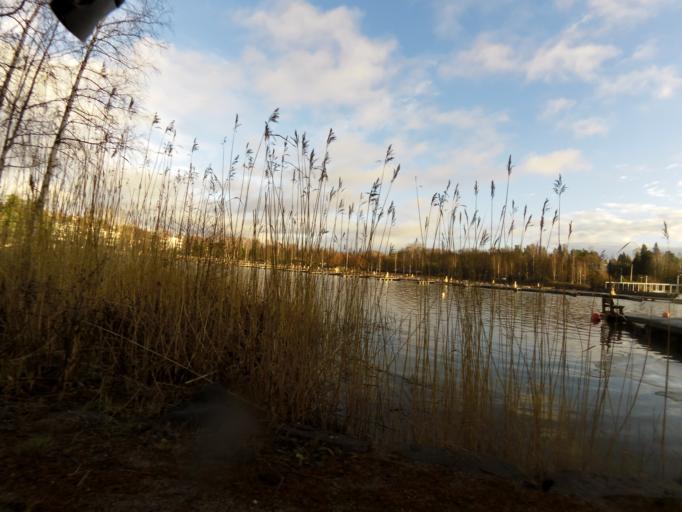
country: FI
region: Uusimaa
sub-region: Helsinki
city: Koukkuniemi
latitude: 60.1559
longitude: 24.7692
